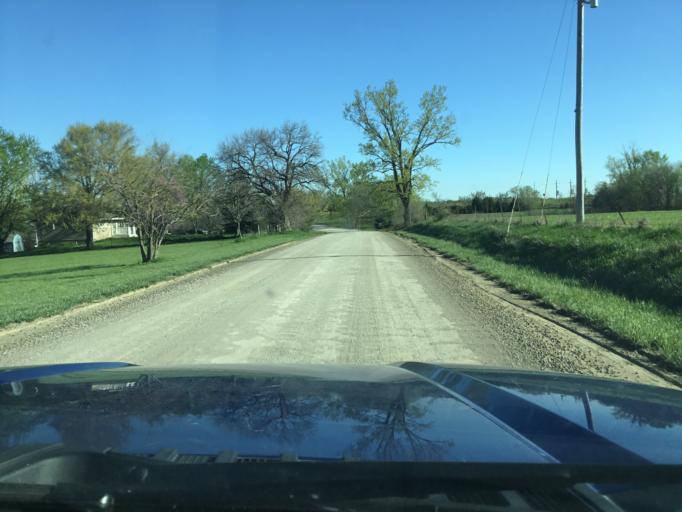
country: US
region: Kansas
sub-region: Douglas County
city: Lawrence
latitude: 38.9690
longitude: -95.3725
